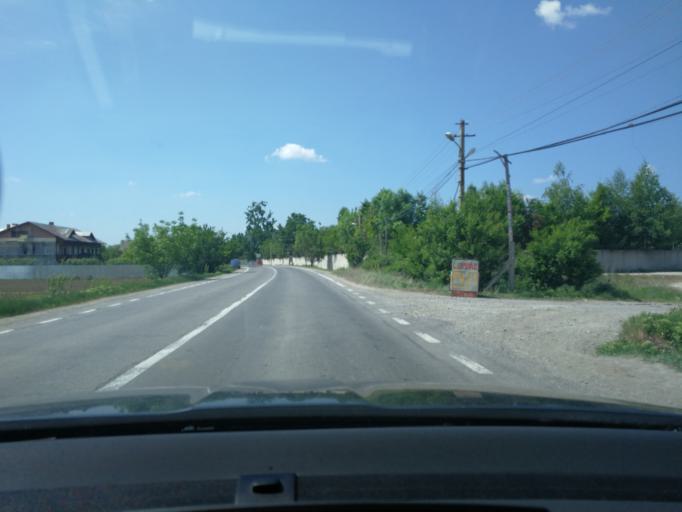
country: RO
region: Prahova
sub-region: Comuna Targsoru Vechi
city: Targsoru Vechi
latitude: 44.8694
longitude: 25.9331
